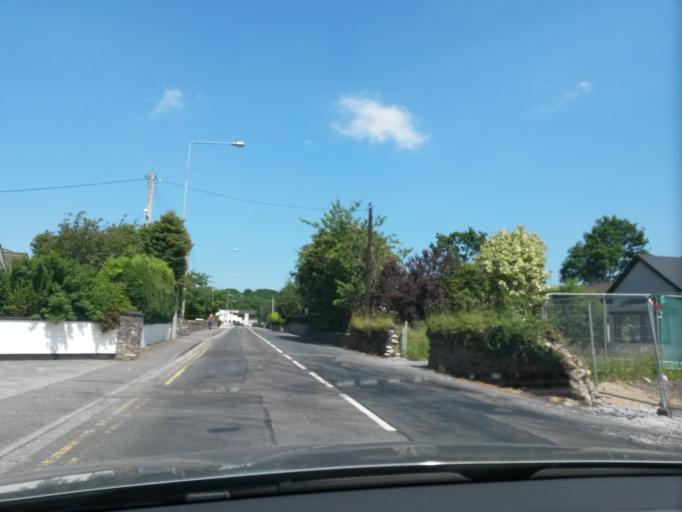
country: IE
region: Munster
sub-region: Ciarrai
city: Cill Airne
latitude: 52.0559
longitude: -9.4809
